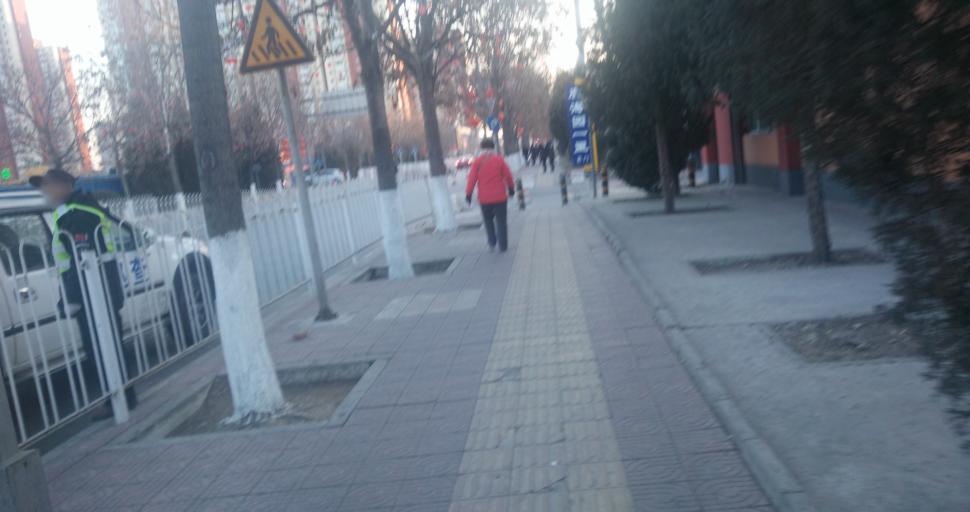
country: CN
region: Beijing
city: Jiugong
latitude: 39.7607
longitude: 116.4970
